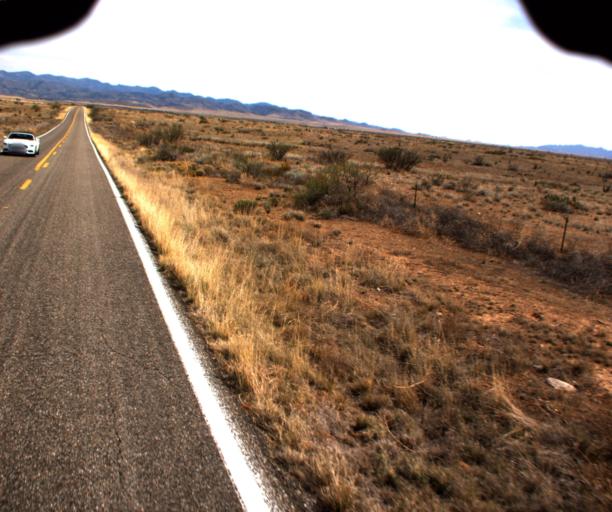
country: US
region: Arizona
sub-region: Cochise County
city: Willcox
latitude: 32.0614
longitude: -109.5023
